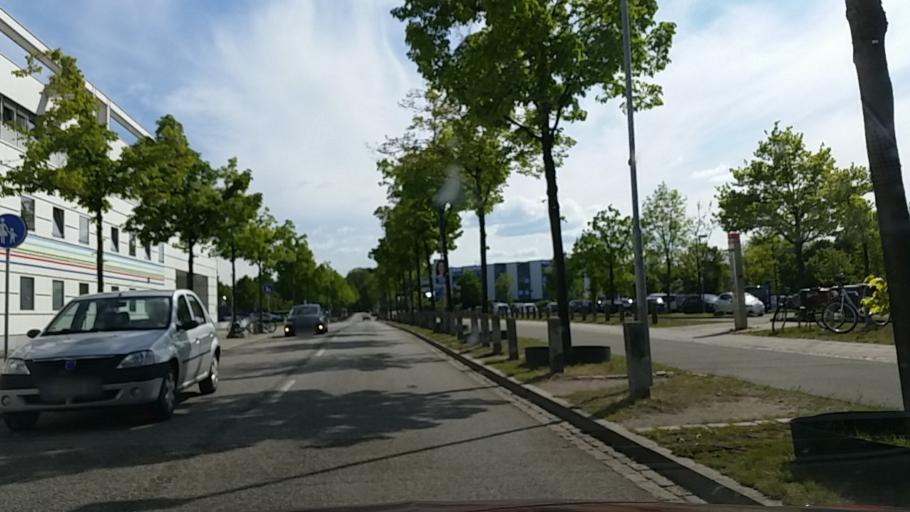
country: DE
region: Schleswig-Holstein
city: Luebeck
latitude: 53.8694
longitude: 10.6775
